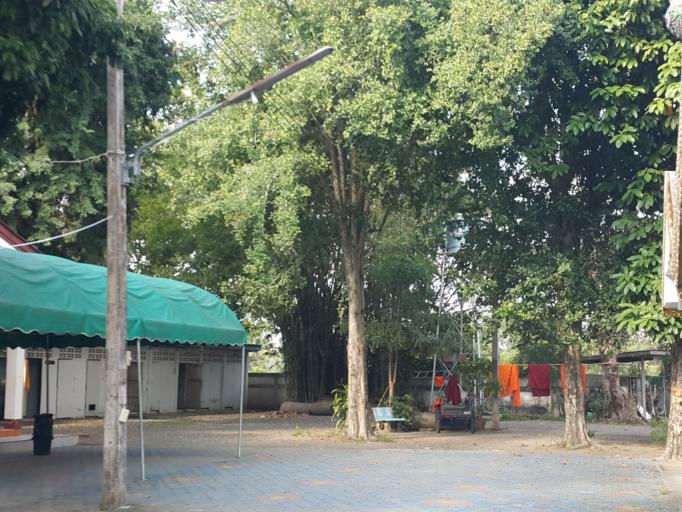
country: TH
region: Chiang Mai
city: San Kamphaeng
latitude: 18.8110
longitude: 99.1184
